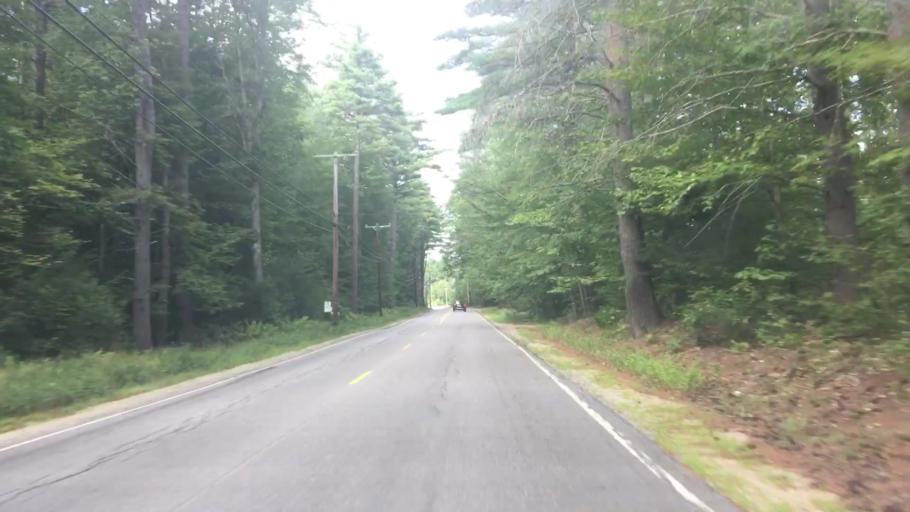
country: US
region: Maine
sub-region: Oxford County
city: Oxford
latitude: 44.1180
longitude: -70.5057
